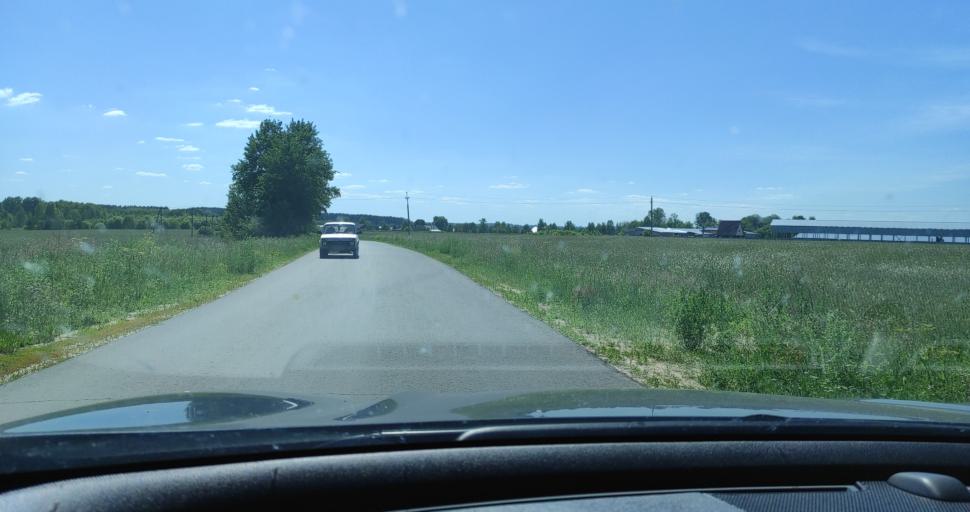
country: RU
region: Rjazan
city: Murmino
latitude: 54.5697
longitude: 40.0972
